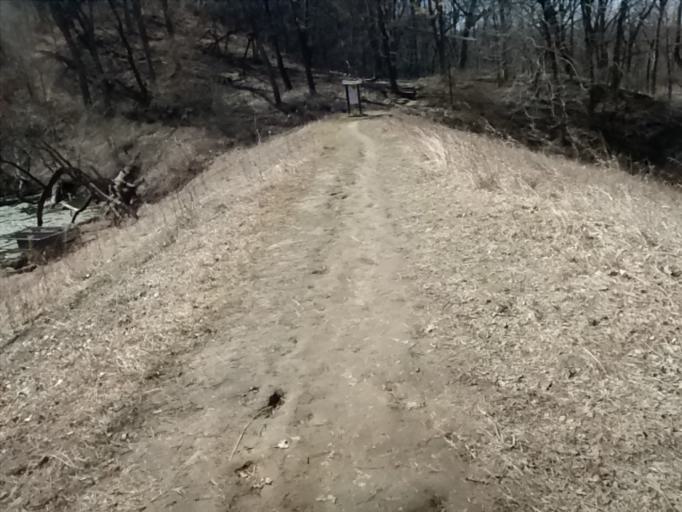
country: US
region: Nebraska
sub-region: Sarpy County
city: Bellevue
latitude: 41.1827
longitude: -95.9111
